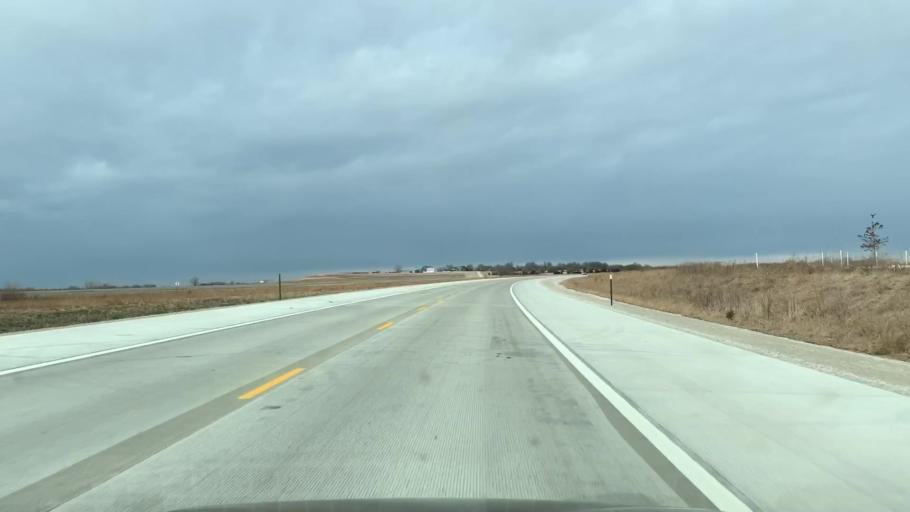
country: US
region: Kansas
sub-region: Allen County
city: Humboldt
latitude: 37.8503
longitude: -95.4098
